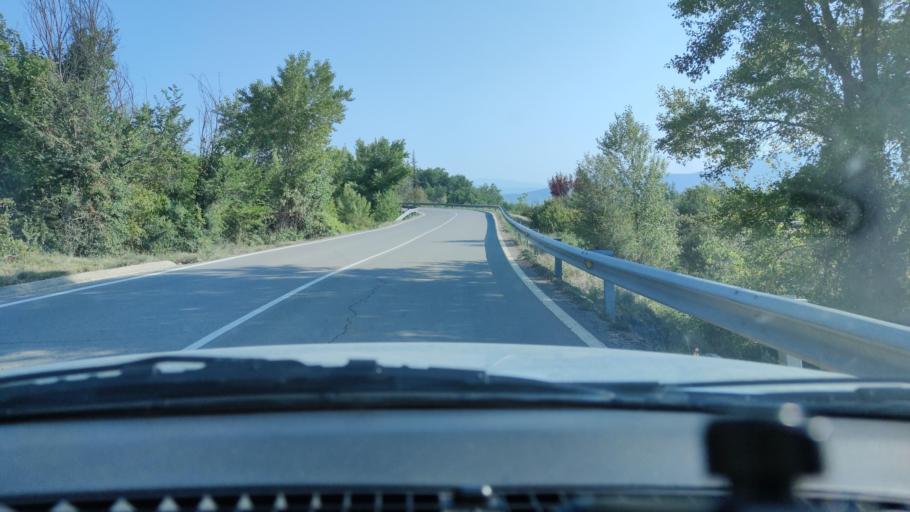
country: ES
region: Catalonia
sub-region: Provincia de Lleida
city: Llimiana
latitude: 42.0964
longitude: 0.8864
